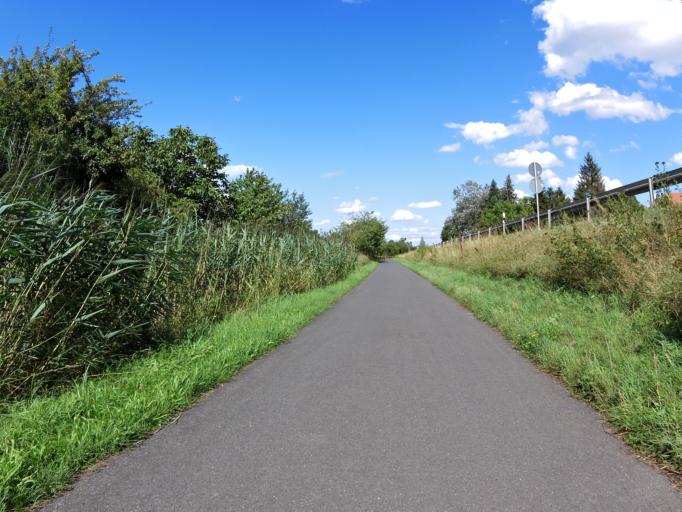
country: DE
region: Bavaria
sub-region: Regierungsbezirk Unterfranken
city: Kitzingen
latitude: 49.7180
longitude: 10.1536
